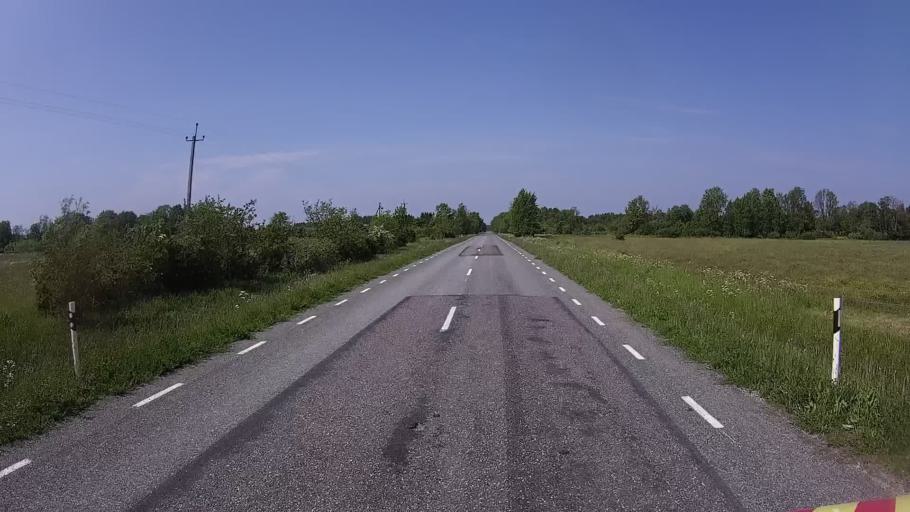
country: EE
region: Saare
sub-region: Kuressaare linn
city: Kuressaare
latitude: 58.3690
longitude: 22.0488
